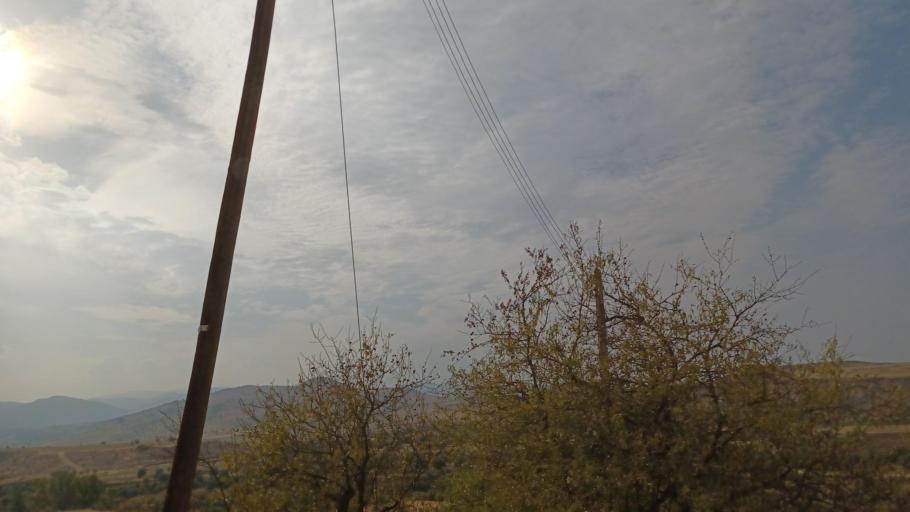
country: CY
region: Lefkosia
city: Peristerona
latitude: 35.0747
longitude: 33.0918
